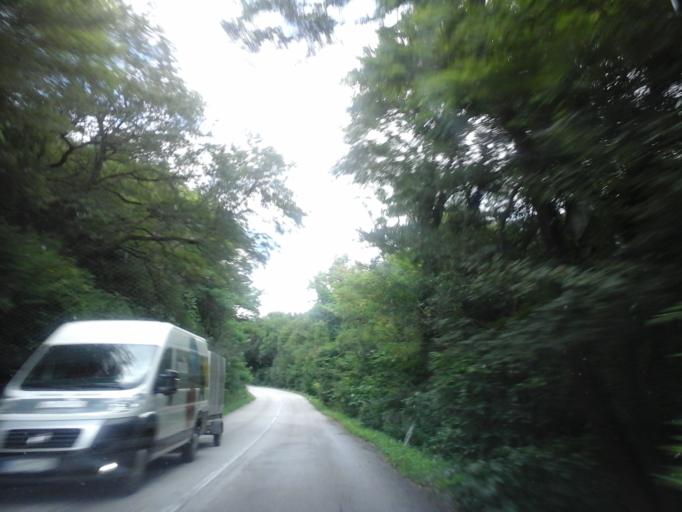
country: SK
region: Kosicky
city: Roznava
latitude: 48.5533
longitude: 20.4006
